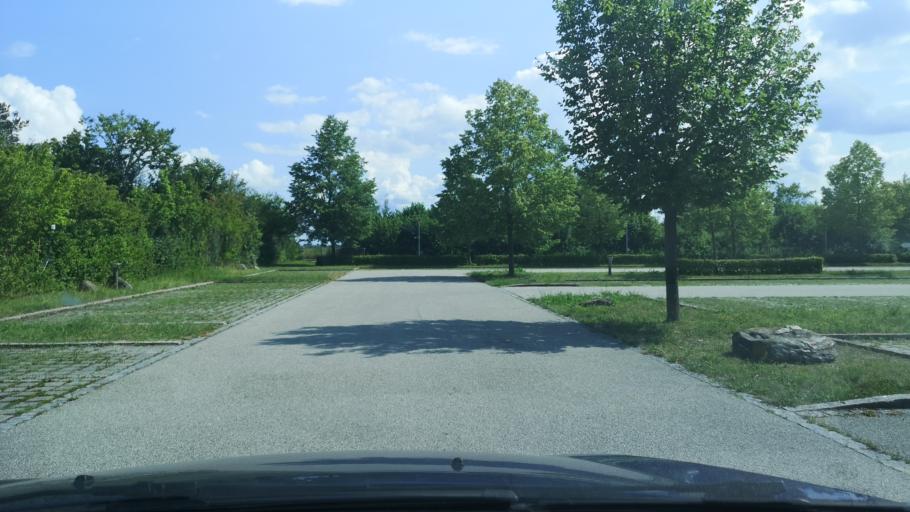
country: DE
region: Bavaria
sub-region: Upper Bavaria
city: Kirchheim bei Muenchen
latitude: 48.1641
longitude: 11.7781
